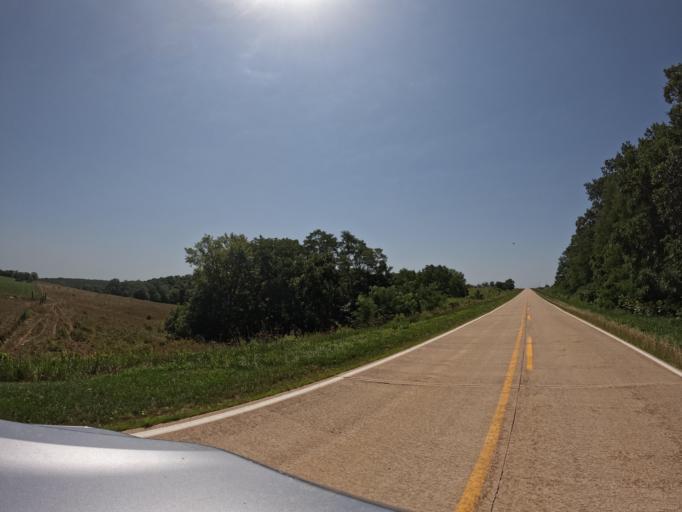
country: US
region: Iowa
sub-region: Henry County
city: Mount Pleasant
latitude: 40.8752
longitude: -91.5602
